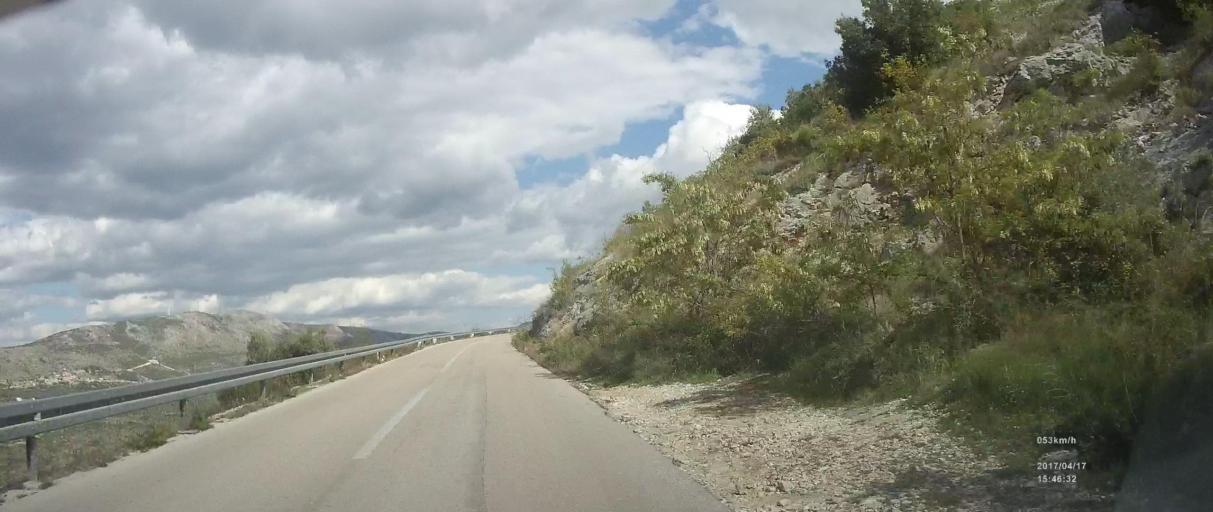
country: HR
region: Sibensko-Kniniska
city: Primosten
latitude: 43.6269
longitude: 15.9730
